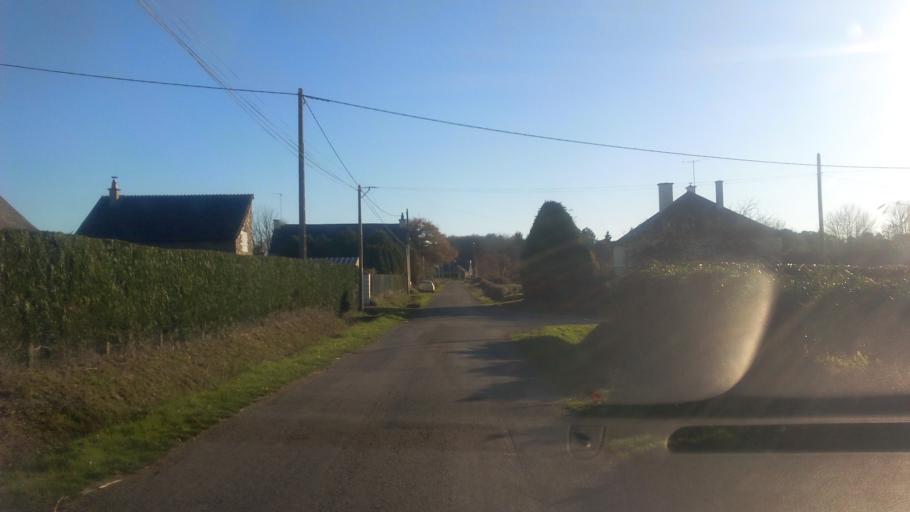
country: FR
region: Brittany
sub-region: Departement du Morbihan
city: Peillac
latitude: 47.7243
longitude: -2.2290
